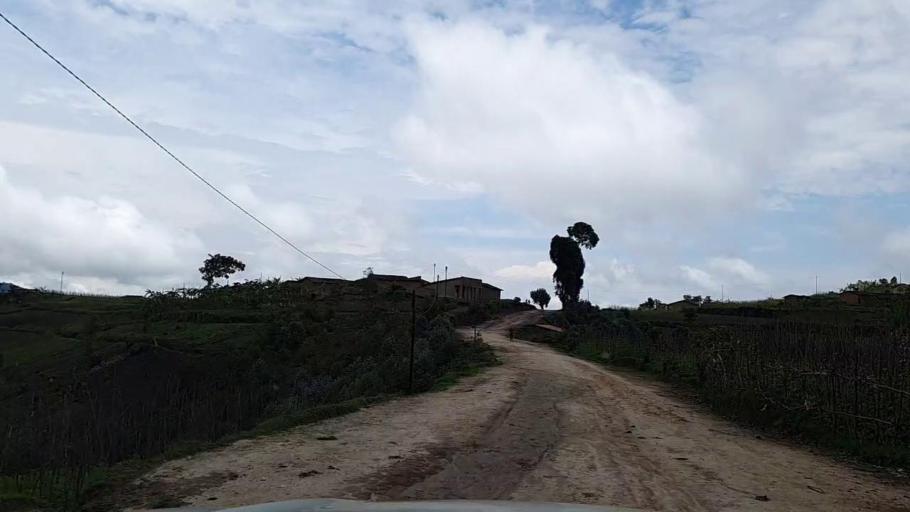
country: RW
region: Southern Province
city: Gikongoro
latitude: -2.3460
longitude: 29.5064
